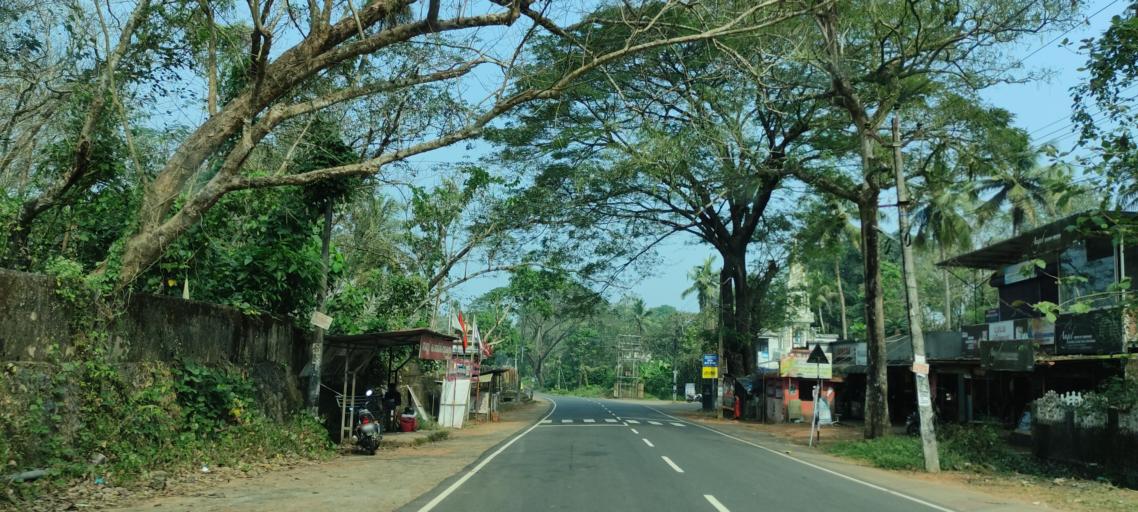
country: IN
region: Kerala
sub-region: Ernakulam
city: Piravam
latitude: 9.8020
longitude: 76.4802
